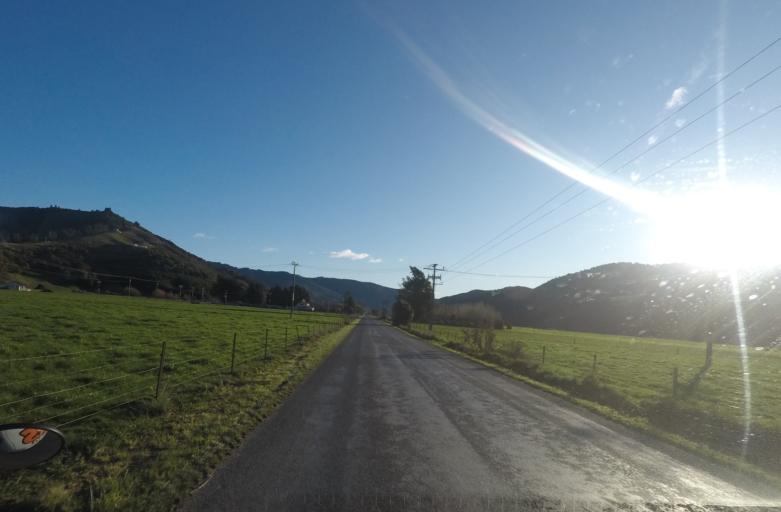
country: NZ
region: Marlborough
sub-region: Marlborough District
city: Picton
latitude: -41.2893
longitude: 173.8615
